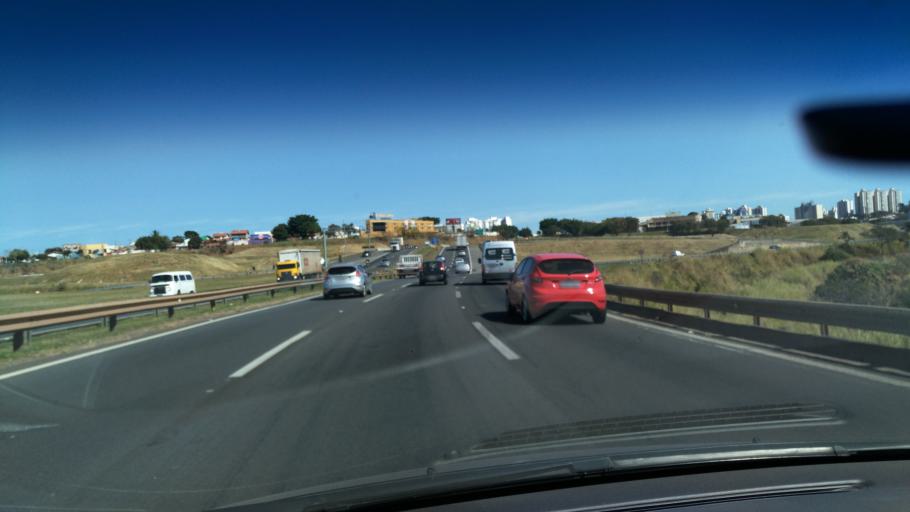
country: BR
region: Sao Paulo
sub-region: Campinas
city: Campinas
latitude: -22.8419
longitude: -47.0371
